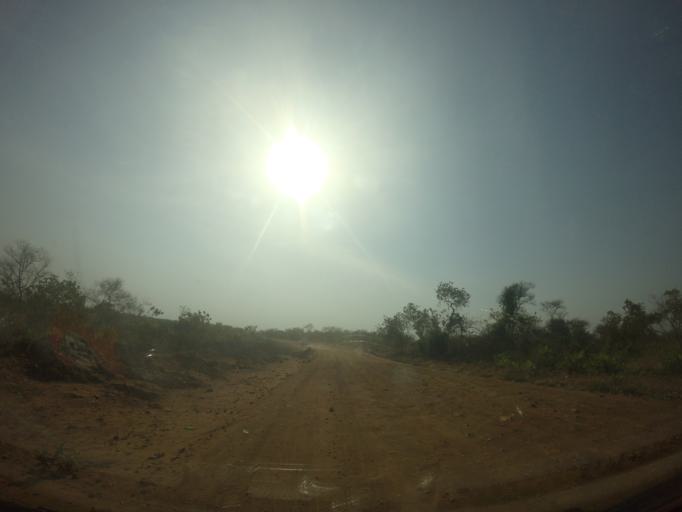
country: UG
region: Northern Region
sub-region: Maracha District
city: Maracha
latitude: 3.1141
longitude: 31.1924
